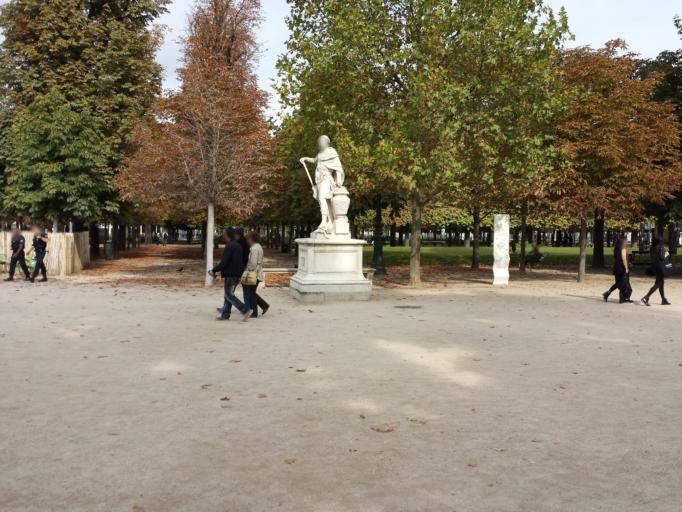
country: FR
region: Ile-de-France
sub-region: Paris
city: Paris
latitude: 48.8644
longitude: 2.3248
